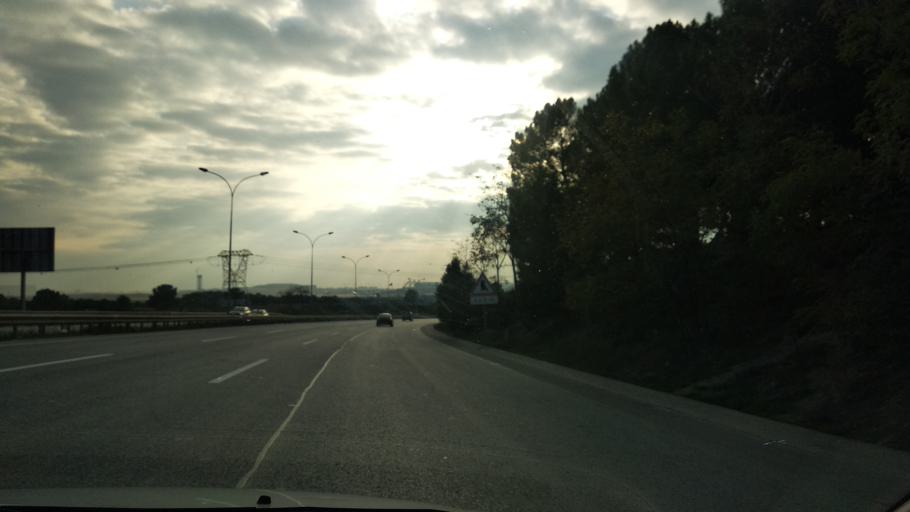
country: TR
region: Istanbul
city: Pendik
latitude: 40.9177
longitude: 29.3368
